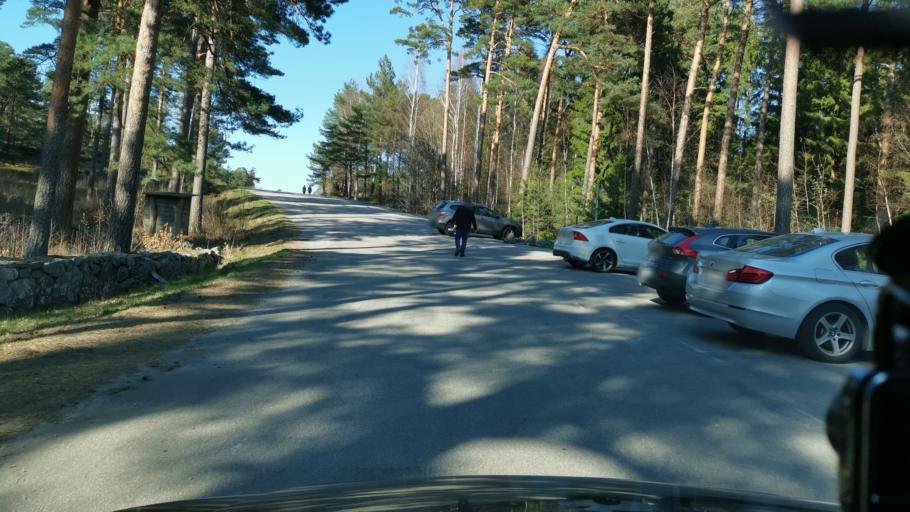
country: SE
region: Vaestra Goetaland
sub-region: Stenungsunds Kommun
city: Stenungsund
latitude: 58.0604
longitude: 11.7998
